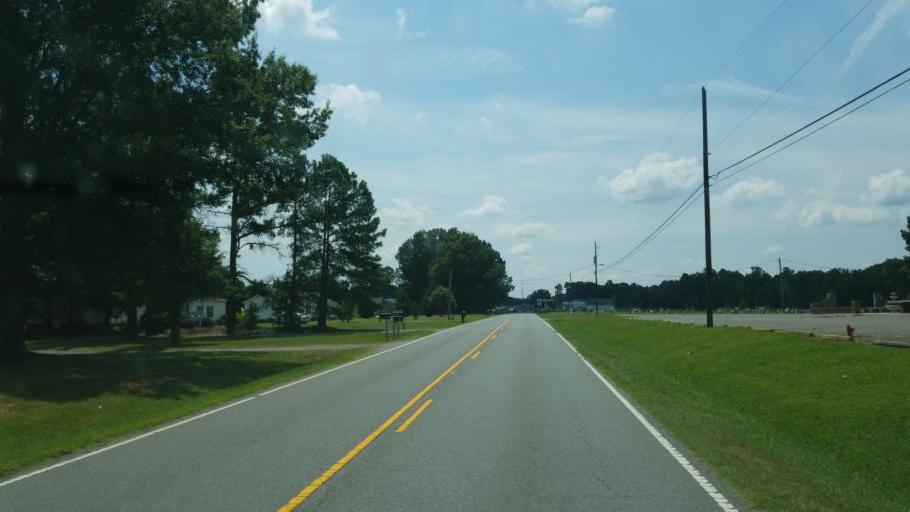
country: US
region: North Carolina
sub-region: Cleveland County
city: Kings Mountain
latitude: 35.2783
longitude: -81.3543
